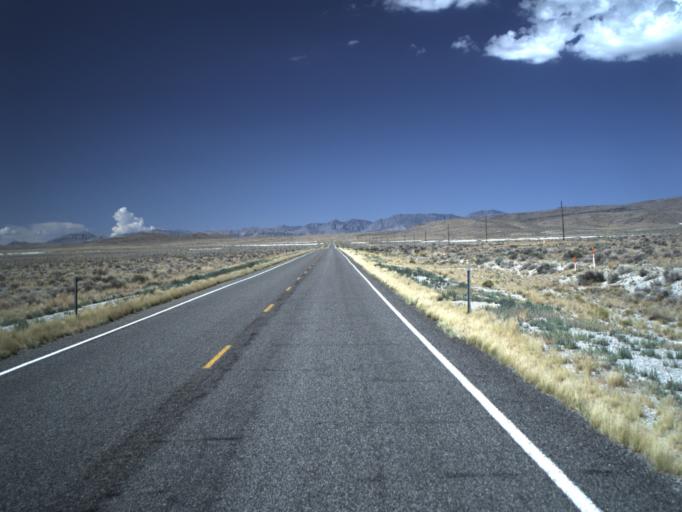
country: US
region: Utah
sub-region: Beaver County
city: Milford
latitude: 39.0687
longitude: -113.2260
